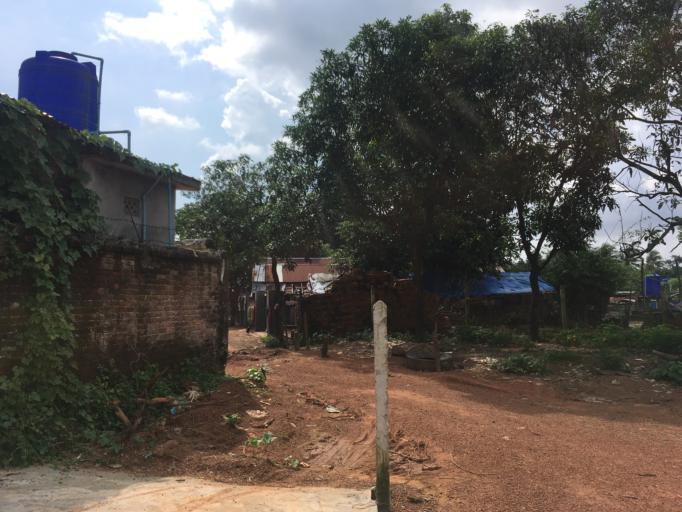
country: MM
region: Mon
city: Mawlamyine
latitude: 16.4578
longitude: 97.6642
